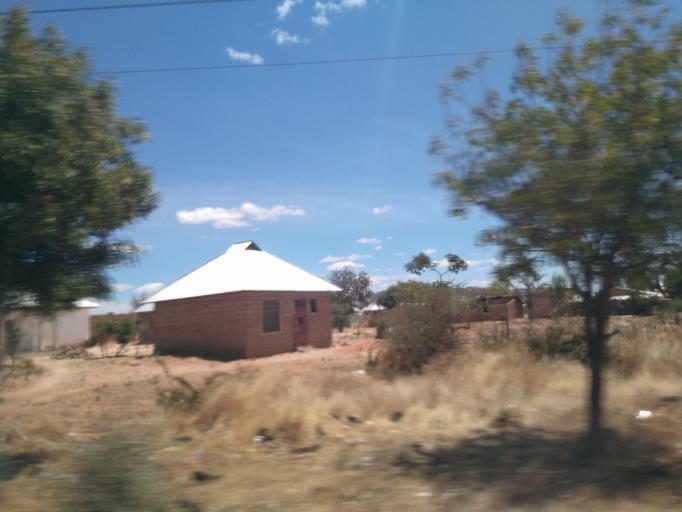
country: TZ
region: Dodoma
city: Kisasa
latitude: -6.1897
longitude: 35.7815
